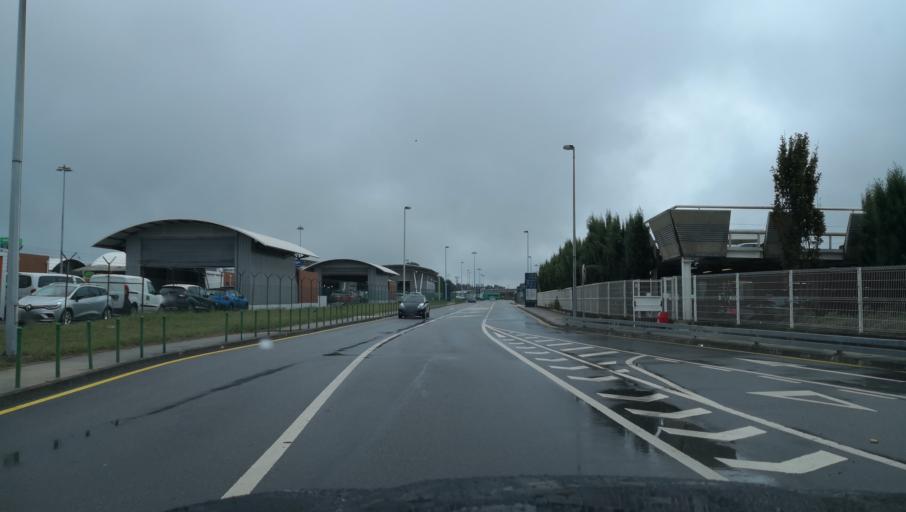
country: PT
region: Porto
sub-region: Matosinhos
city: Santa Cruz do Bispo
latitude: 41.2418
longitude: -8.6701
